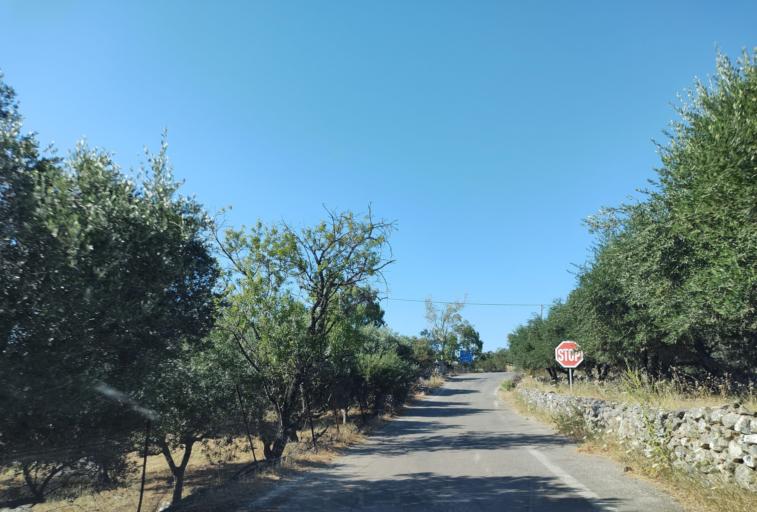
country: GR
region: Crete
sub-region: Nomos Chanias
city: Georgioupolis
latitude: 35.3937
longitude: 24.2359
